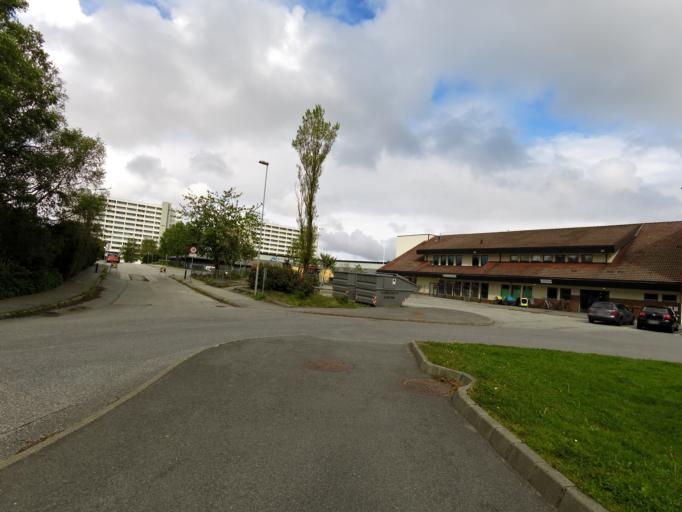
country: NO
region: Rogaland
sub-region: Stavanger
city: Stavanger
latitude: 58.9574
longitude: 5.6968
